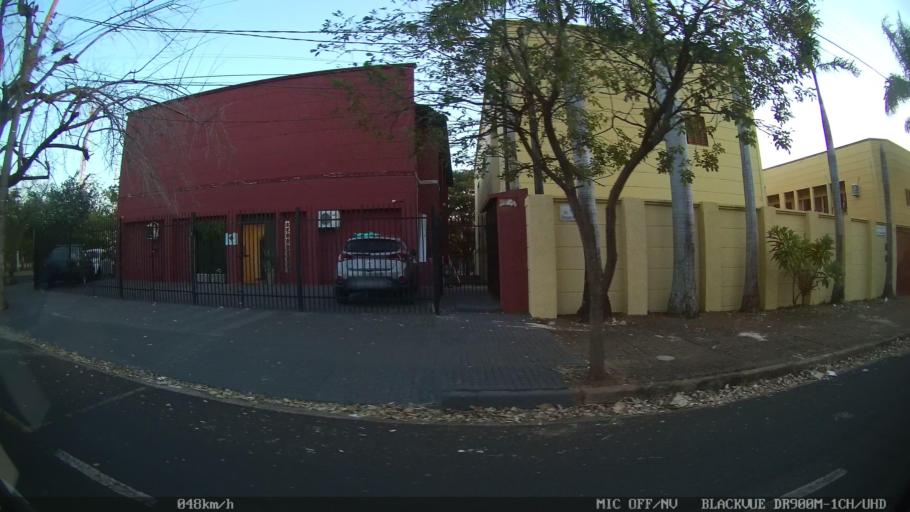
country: BR
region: Sao Paulo
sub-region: Sao Jose Do Rio Preto
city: Sao Jose do Rio Preto
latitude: -20.7990
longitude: -49.3486
